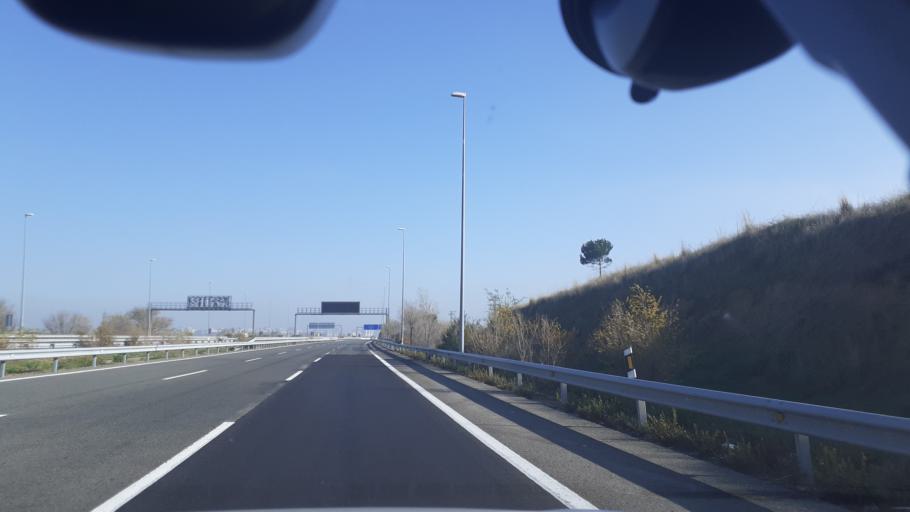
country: ES
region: Madrid
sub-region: Provincia de Madrid
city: Vicalvaro
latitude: 40.4099
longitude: -3.5939
